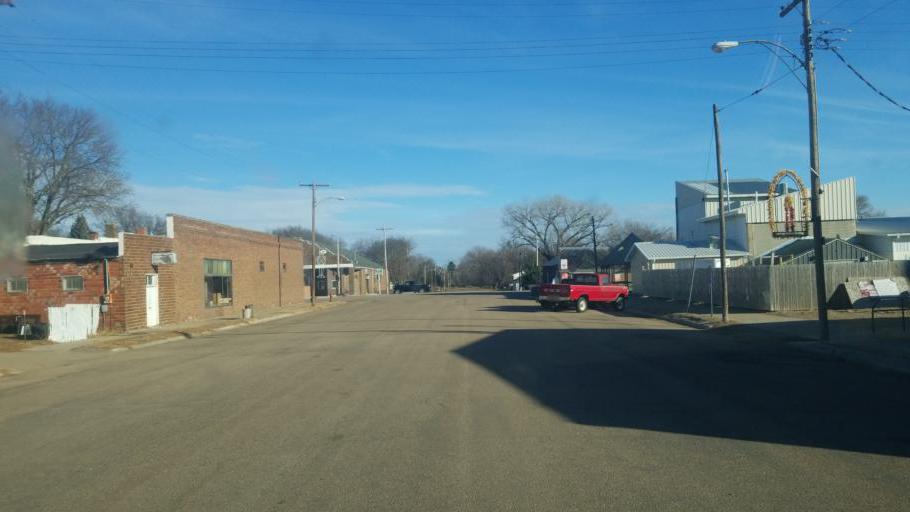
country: US
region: South Dakota
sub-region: Charles Mix County
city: Wagner
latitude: 42.8303
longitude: -98.4672
